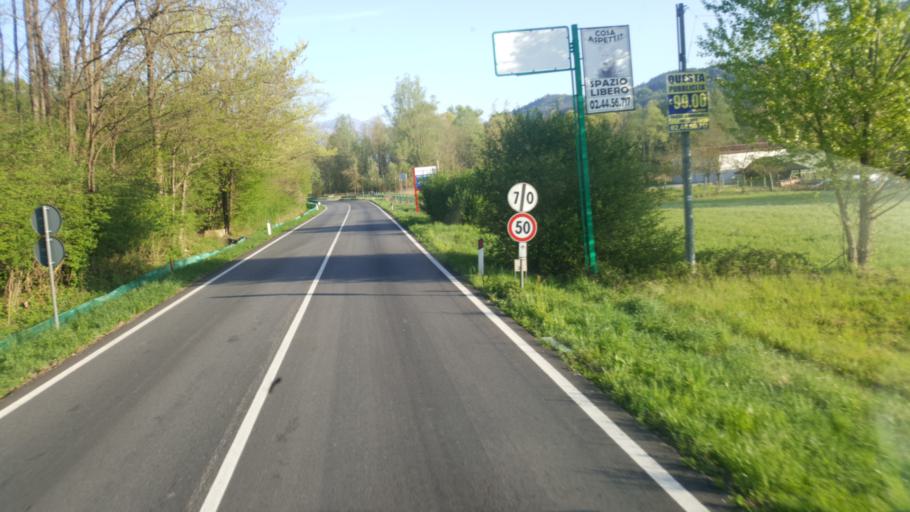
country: IT
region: Lombardy
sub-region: Provincia di Varese
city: Cassano Valcuvia
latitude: 45.9407
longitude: 8.7708
